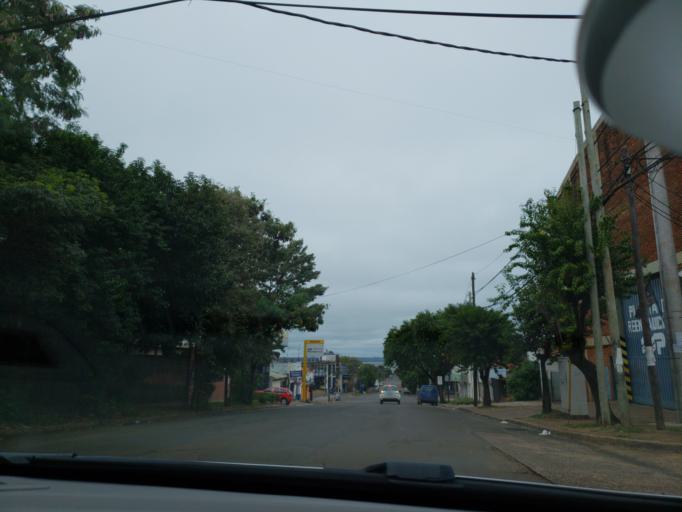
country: AR
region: Misiones
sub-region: Departamento de Capital
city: Posadas
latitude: -27.3942
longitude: -55.9025
